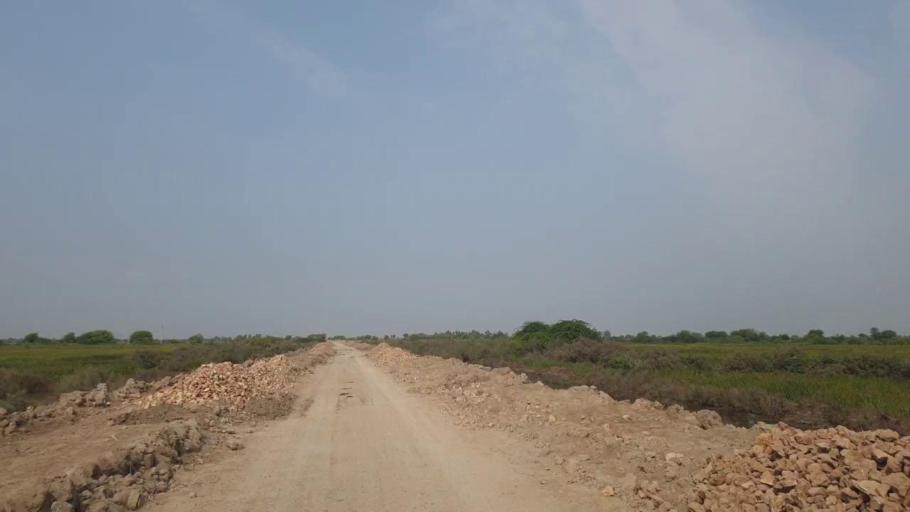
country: PK
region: Sindh
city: Badin
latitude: 24.6078
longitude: 68.7416
